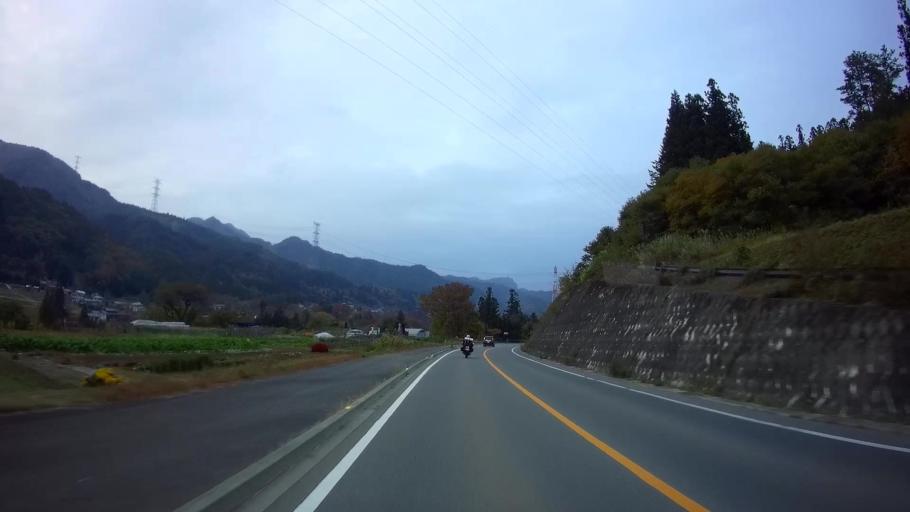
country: JP
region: Gunma
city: Nakanojomachi
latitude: 36.5652
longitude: 138.7446
